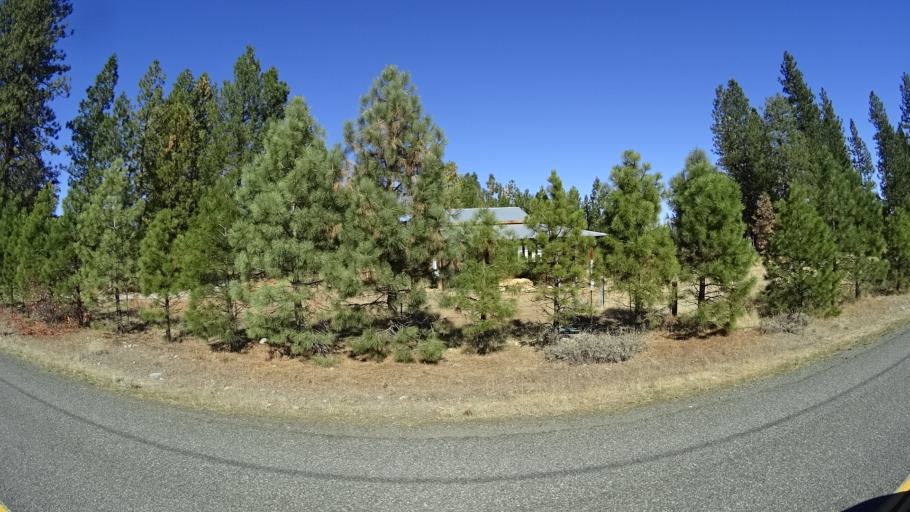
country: US
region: California
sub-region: Siskiyou County
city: Yreka
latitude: 41.5381
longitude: -122.9207
